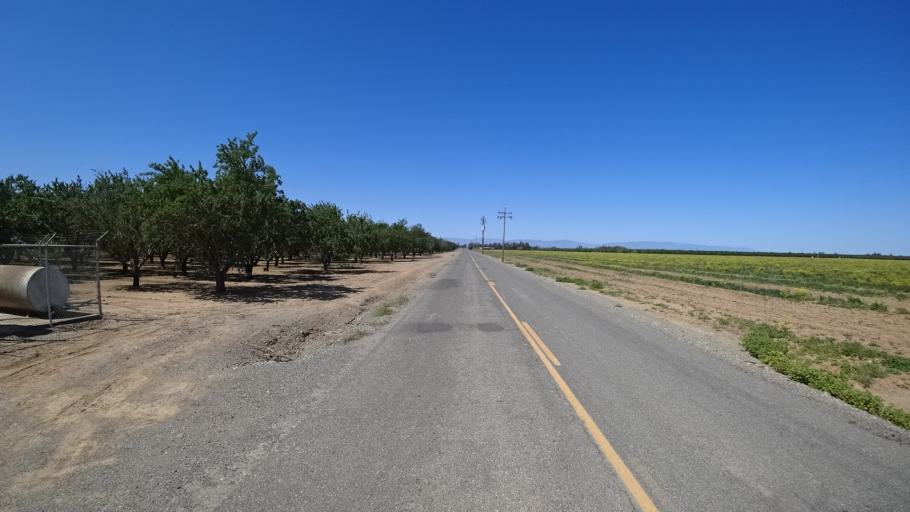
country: US
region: California
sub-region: Glenn County
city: Orland
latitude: 39.6964
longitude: -122.1593
